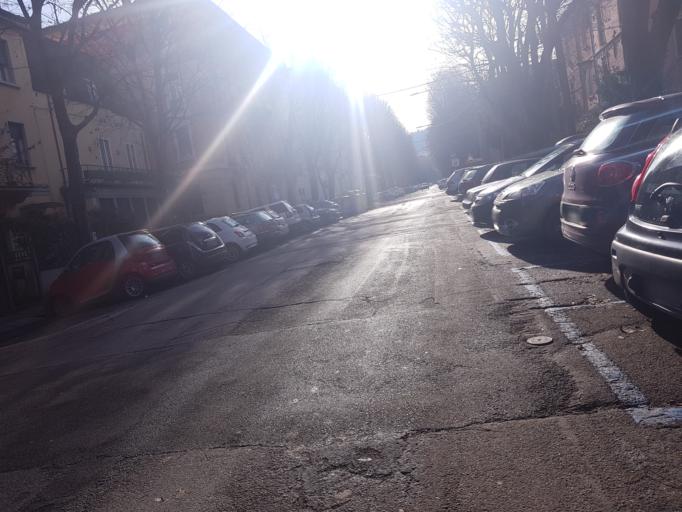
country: IT
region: Emilia-Romagna
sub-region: Provincia di Bologna
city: Bologna
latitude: 44.4941
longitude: 11.3264
